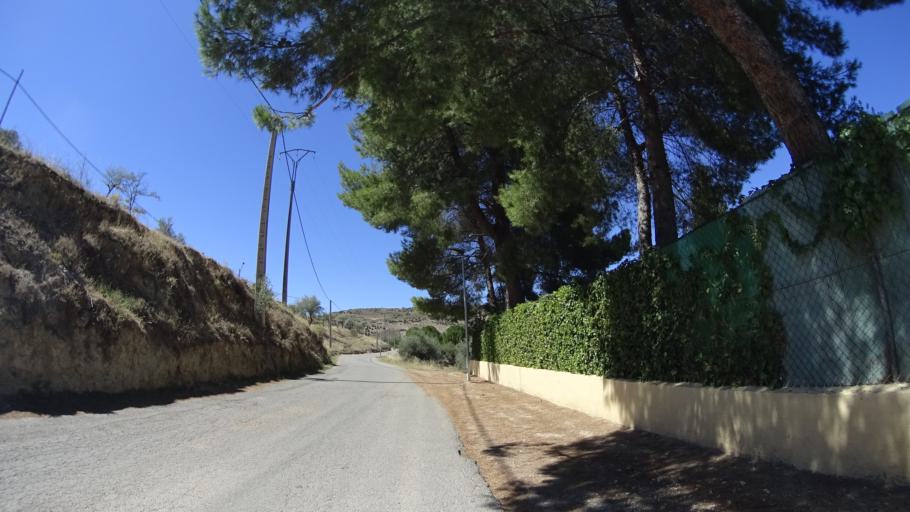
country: ES
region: Madrid
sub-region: Provincia de Madrid
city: Perales de Tajuna
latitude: 40.2275
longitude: -3.3507
